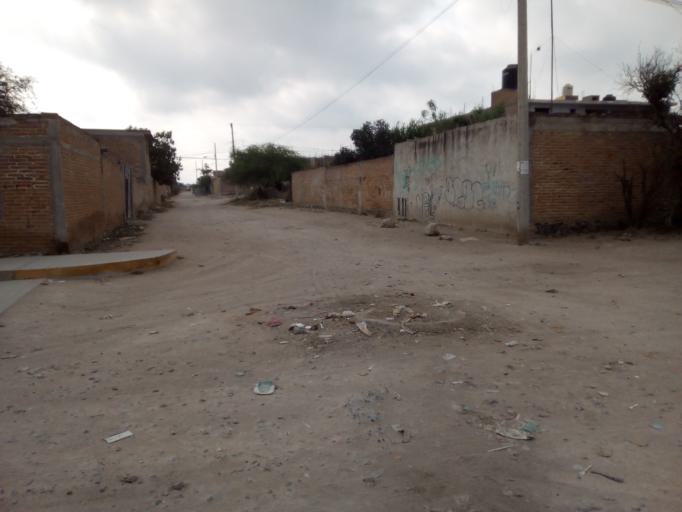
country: MX
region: Guerrero
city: San Luis de la Paz
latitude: 21.2848
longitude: -100.5017
